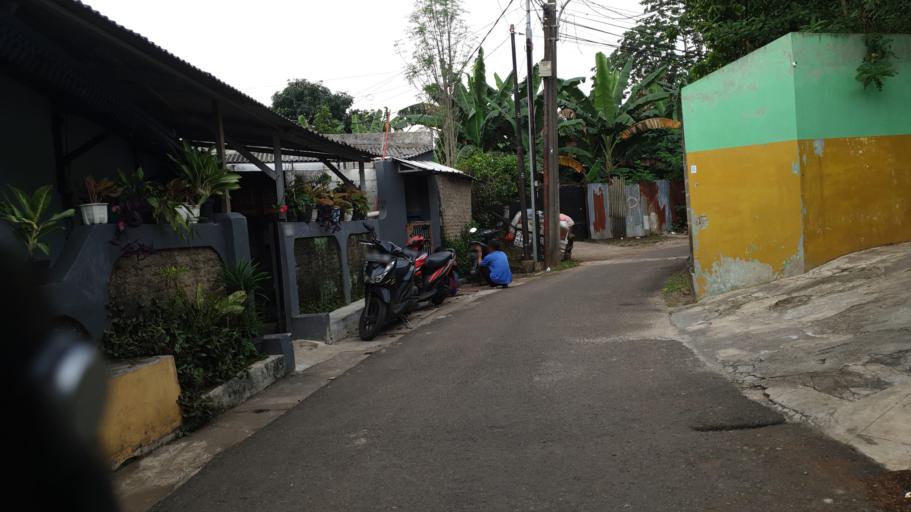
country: ID
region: West Java
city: Depok
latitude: -6.3348
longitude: 106.8255
